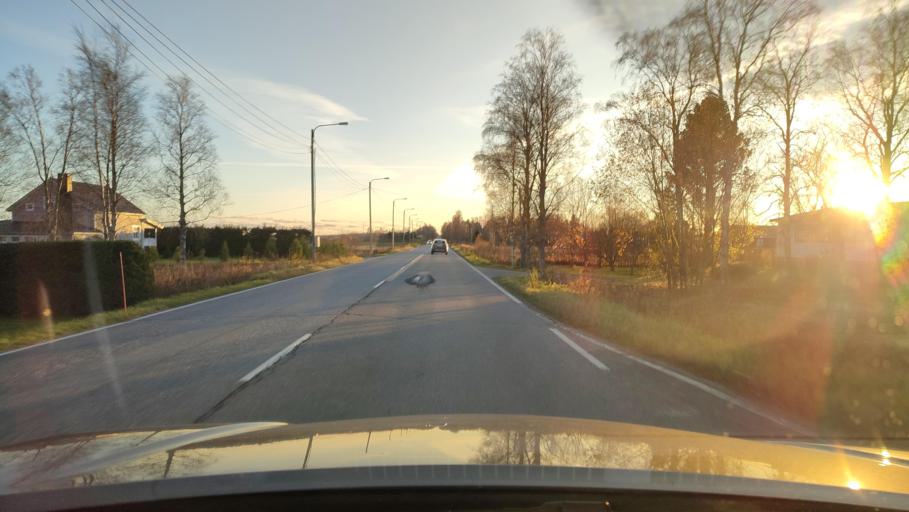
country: FI
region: Ostrobothnia
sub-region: Sydosterbotten
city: Naerpes
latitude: 62.5112
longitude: 21.3610
